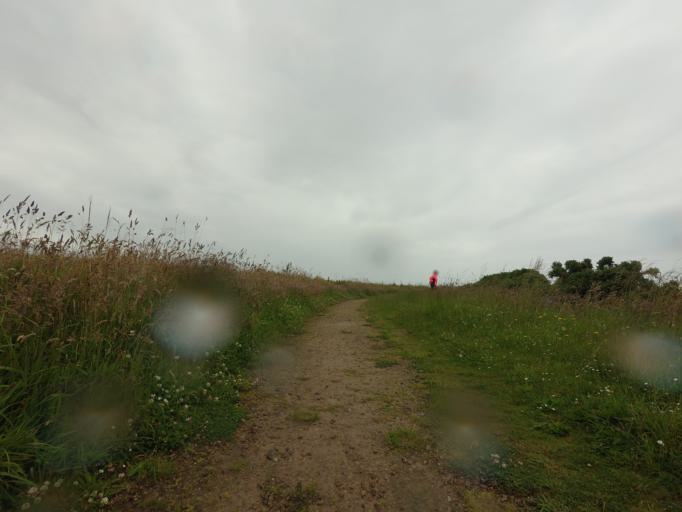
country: GB
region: Scotland
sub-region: Moray
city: Portknockie
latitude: 57.7021
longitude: -2.8725
